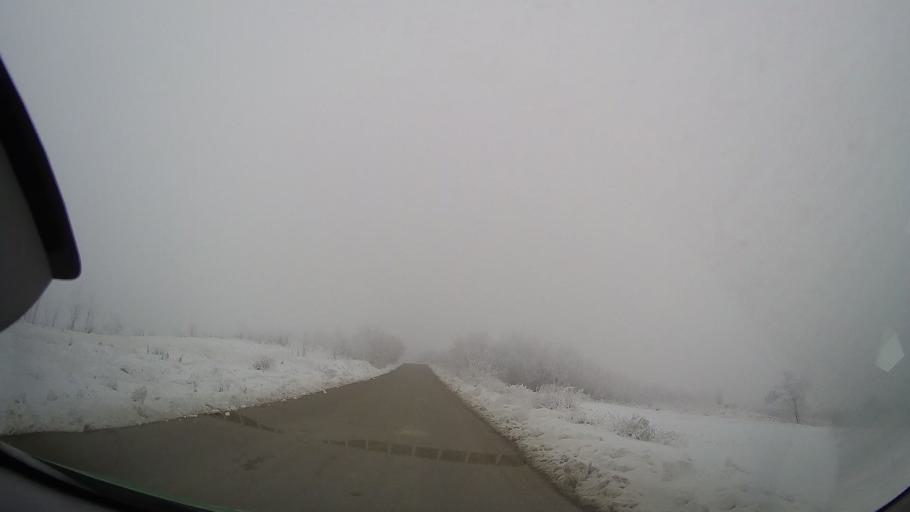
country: RO
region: Iasi
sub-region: Comuna Tansa
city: Suhulet
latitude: 46.8855
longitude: 27.2722
